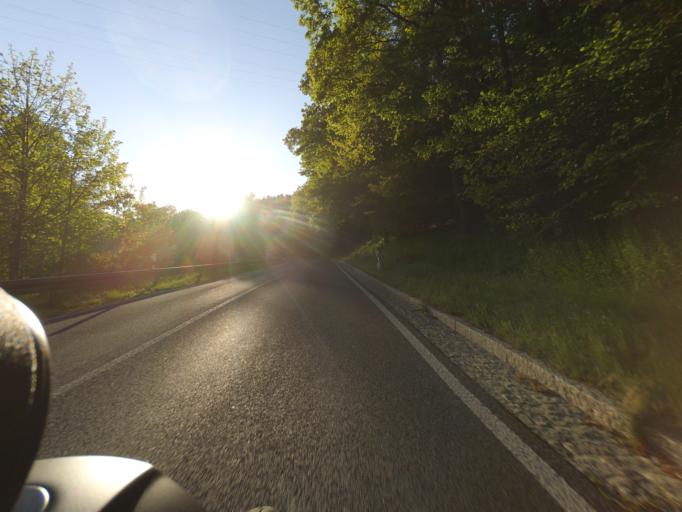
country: DE
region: Saxony
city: Glashutte
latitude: 50.8563
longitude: 13.7619
